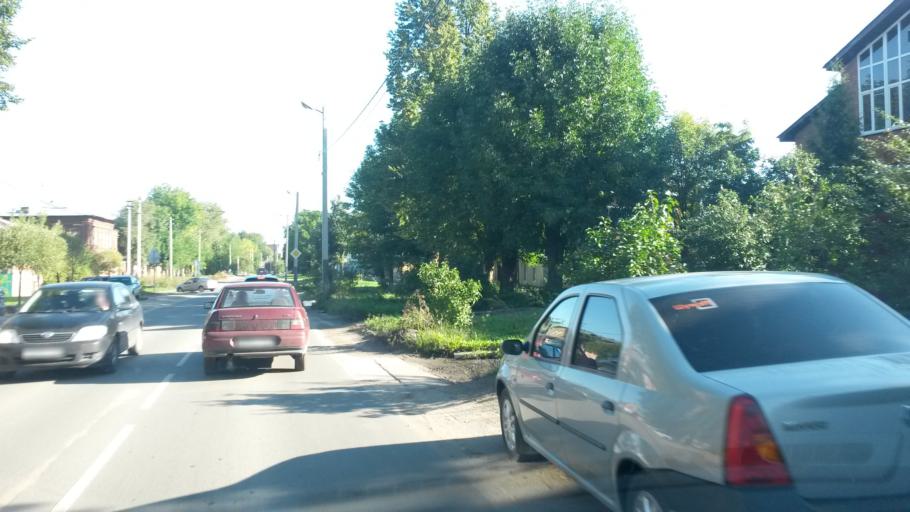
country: RU
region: Ivanovo
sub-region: Gorod Ivanovo
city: Ivanovo
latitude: 56.9892
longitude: 40.9806
